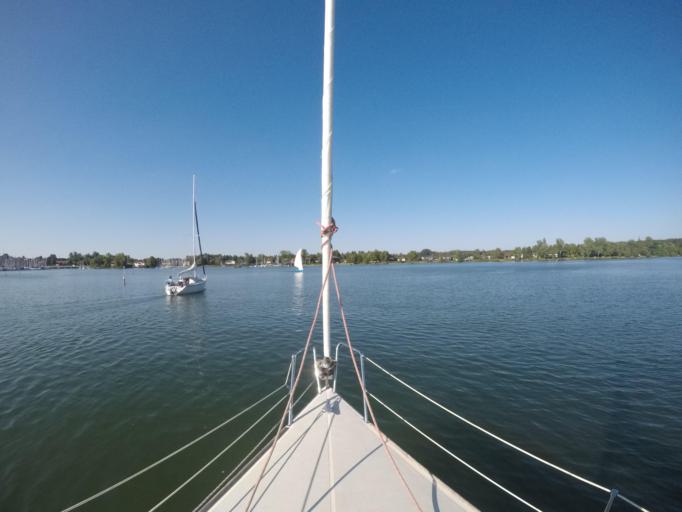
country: DE
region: Bavaria
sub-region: Upper Bavaria
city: Seeon-Seebruck
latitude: 47.9295
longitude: 12.4835
